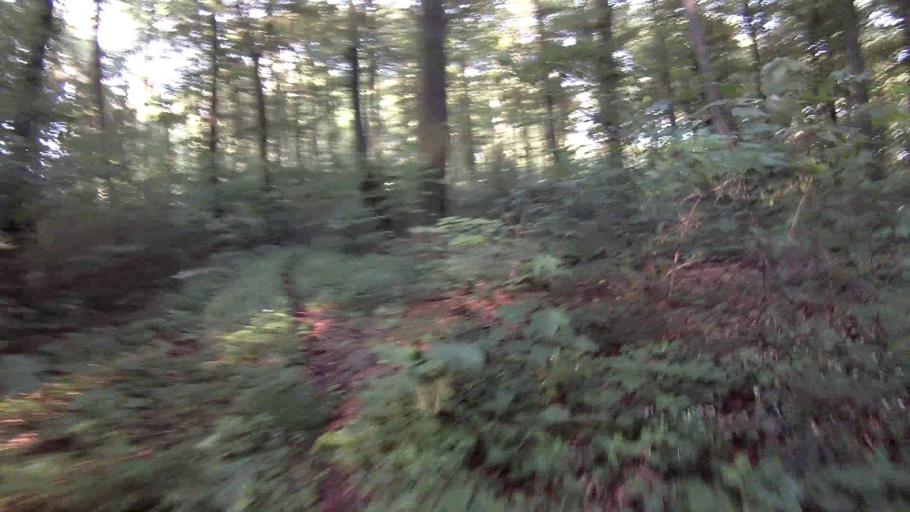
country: DE
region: North Rhine-Westphalia
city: Bad Lippspringe
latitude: 51.7304
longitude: 8.8590
